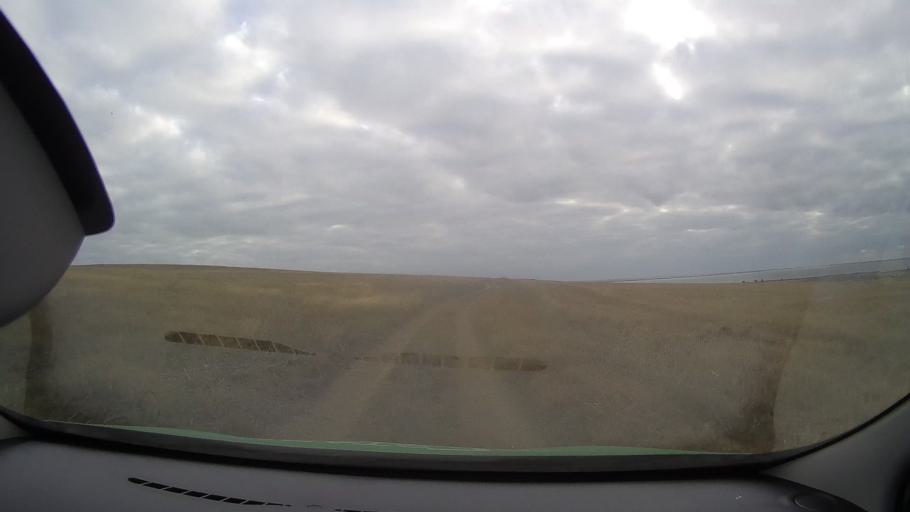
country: RO
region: Tulcea
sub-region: Comuna Jurilovca
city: Jurilovca
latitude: 44.7647
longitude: 28.9260
